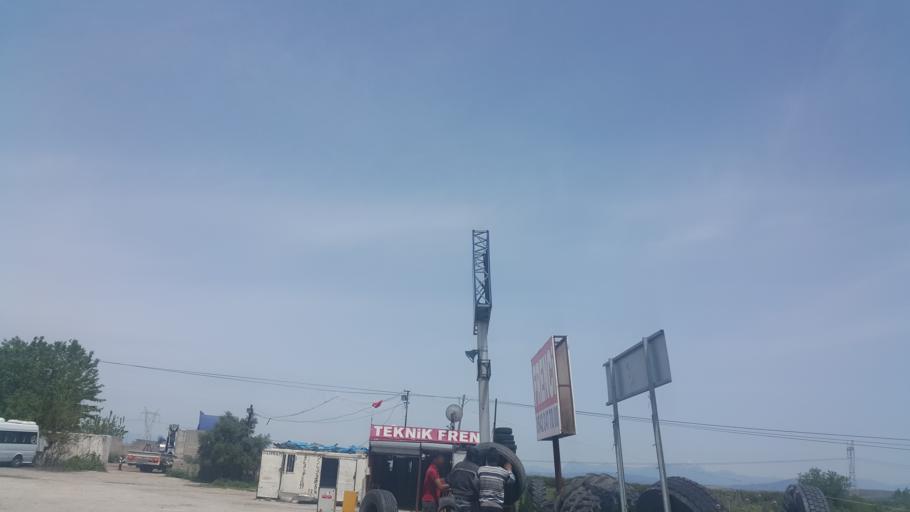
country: TR
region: Osmaniye
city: Toprakkale
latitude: 37.0615
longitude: 36.1123
